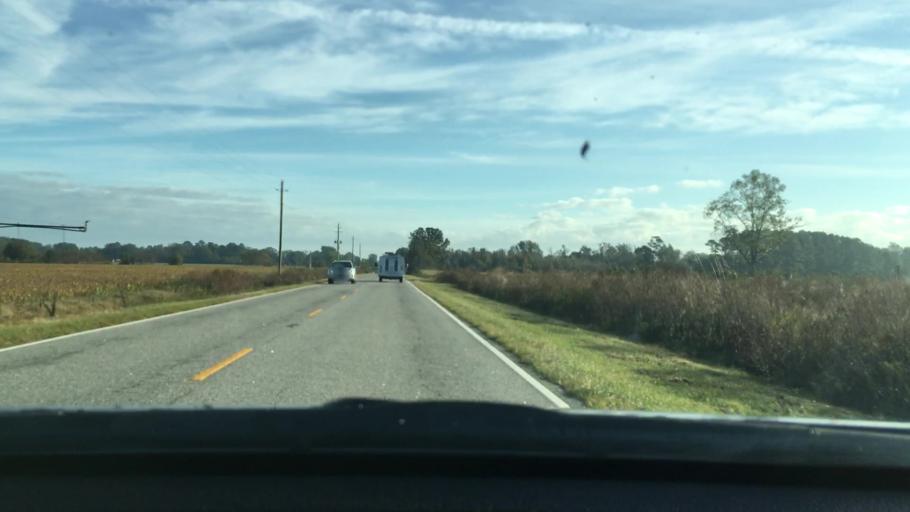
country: US
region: South Carolina
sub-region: Sumter County
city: East Sumter
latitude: 34.0614
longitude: -80.2274
